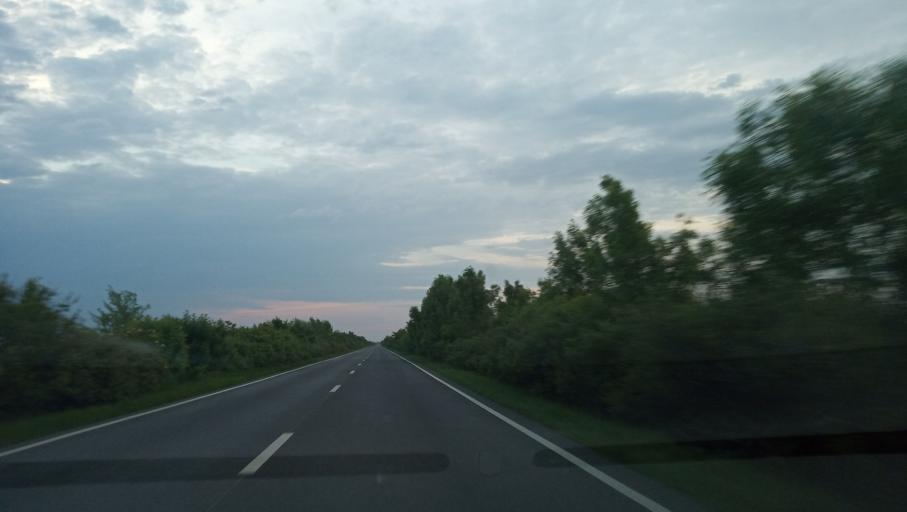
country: RO
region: Timis
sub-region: Comuna Jebel
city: Jebel
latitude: 45.5296
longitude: 21.2302
